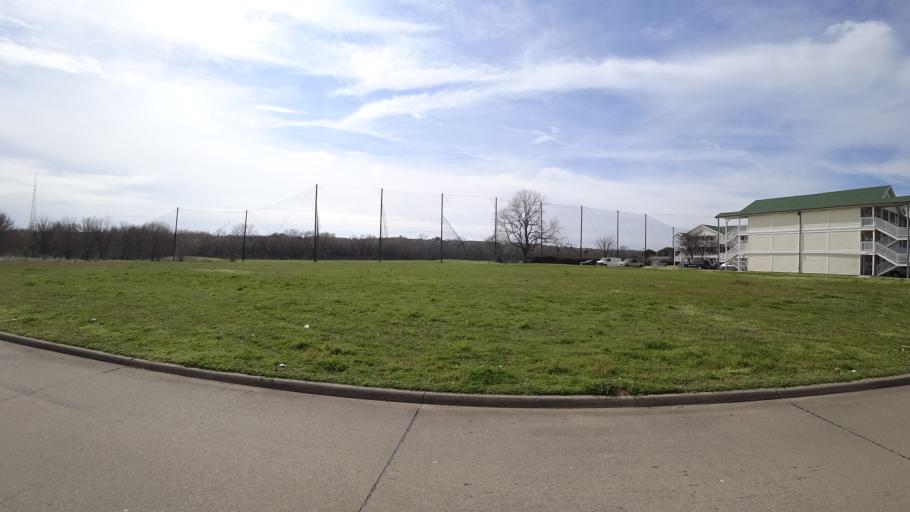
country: US
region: Texas
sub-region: Denton County
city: Lewisville
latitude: 33.0155
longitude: -96.9835
